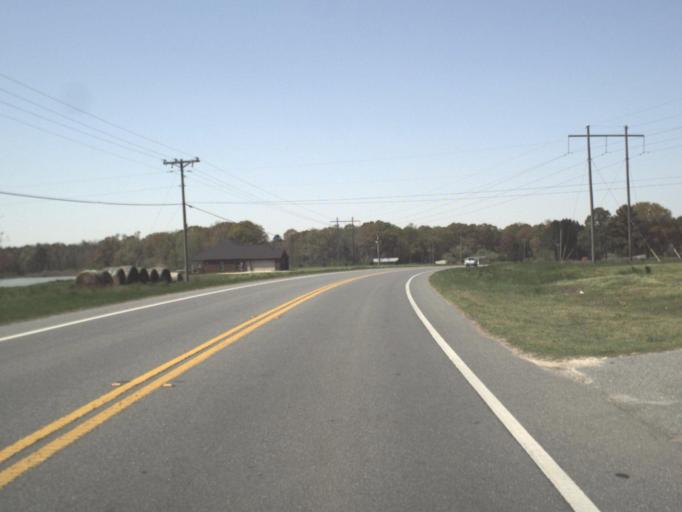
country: US
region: Florida
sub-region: Jackson County
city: Graceville
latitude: 30.9635
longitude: -85.5832
